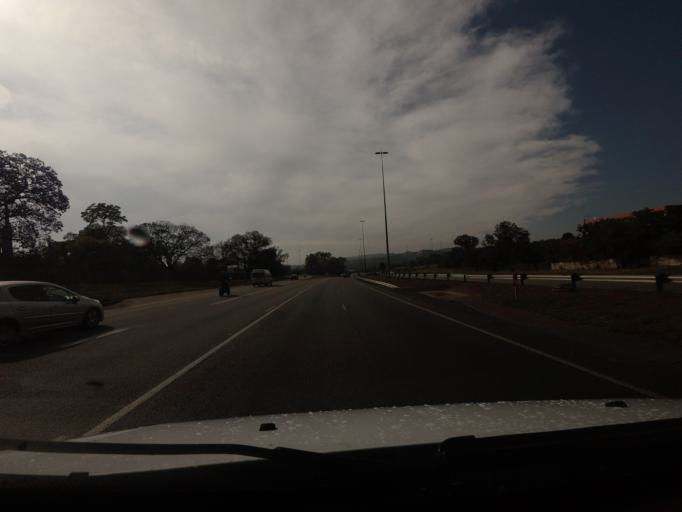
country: ZA
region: Gauteng
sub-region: City of Tshwane Metropolitan Municipality
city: Pretoria
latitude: -25.7434
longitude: 28.2897
